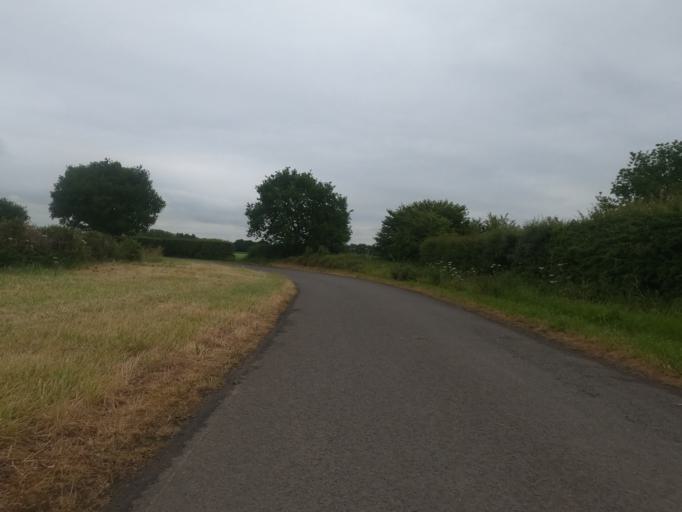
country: GB
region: England
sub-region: Cheshire West and Chester
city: Marston
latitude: 53.2391
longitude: -2.4886
